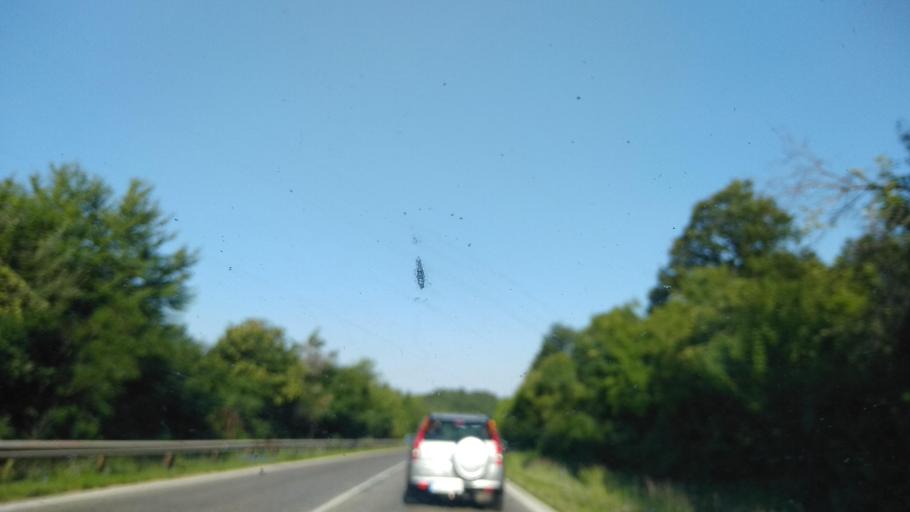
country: BG
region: Lovech
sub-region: Obshtina Lovech
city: Lovech
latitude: 43.0488
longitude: 24.7983
